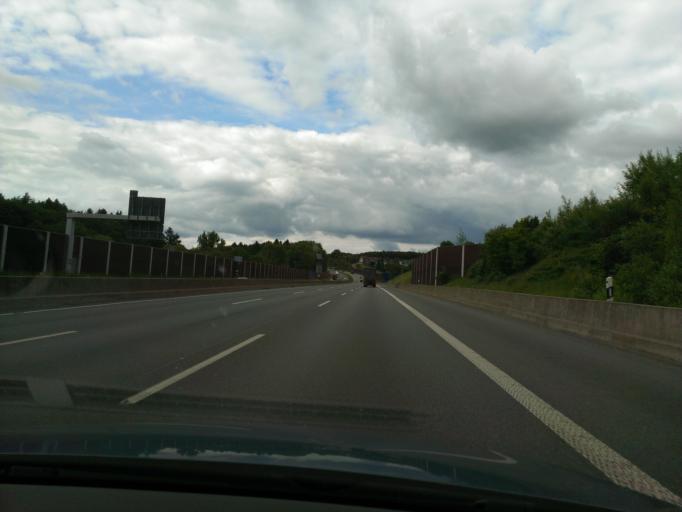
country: DE
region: North Rhine-Westphalia
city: Wermelskirchen
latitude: 51.1641
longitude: 7.2333
